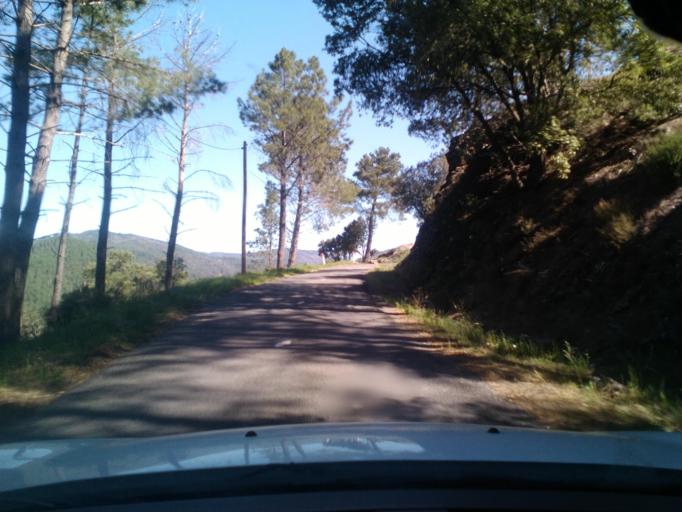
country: FR
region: Languedoc-Roussillon
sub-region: Departement du Gard
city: Valleraugue
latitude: 44.1712
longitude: 3.7515
